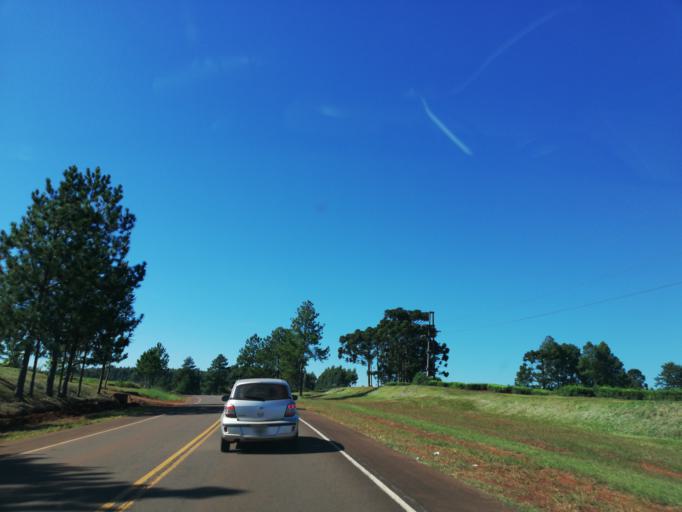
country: AR
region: Misiones
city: Dos de Mayo
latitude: -27.0679
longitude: -54.4160
